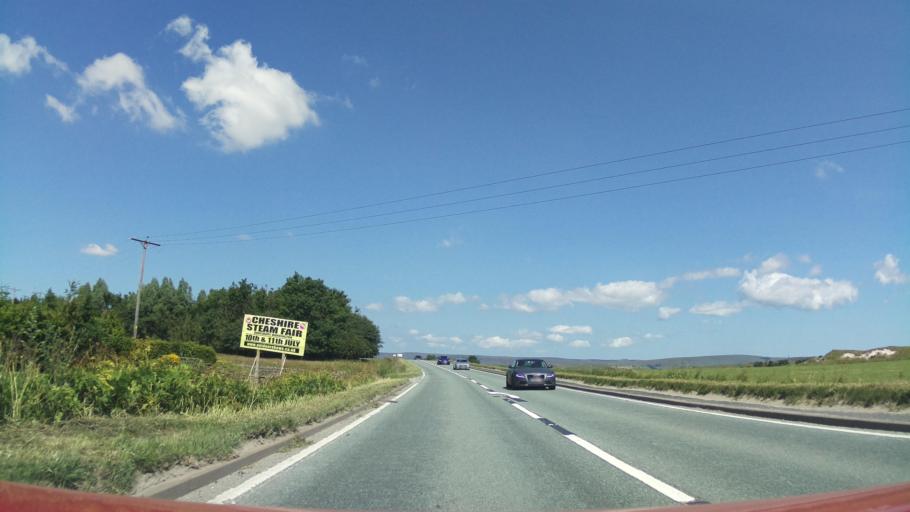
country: GB
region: England
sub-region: Derbyshire
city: Buxton
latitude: 53.2854
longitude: -1.8896
